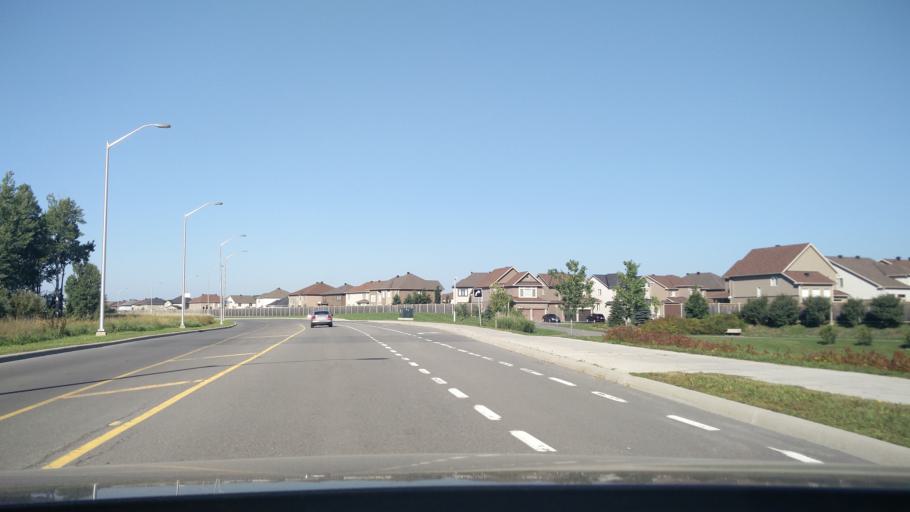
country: CA
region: Ontario
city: Clarence-Rockland
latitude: 45.4572
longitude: -75.4519
